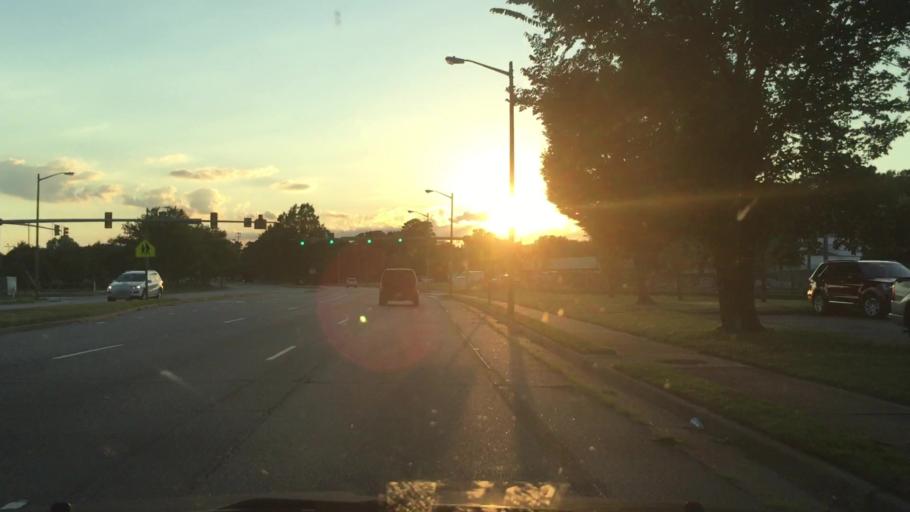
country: US
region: Virginia
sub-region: City of Portsmouth
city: Portsmouth
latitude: 36.8371
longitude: -76.3176
